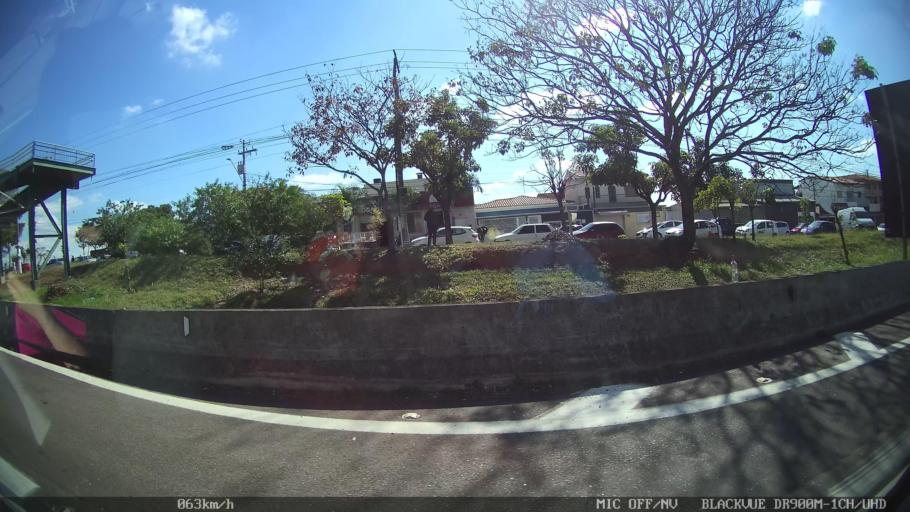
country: BR
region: Sao Paulo
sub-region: Hortolandia
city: Hortolandia
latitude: -22.8995
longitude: -47.1966
